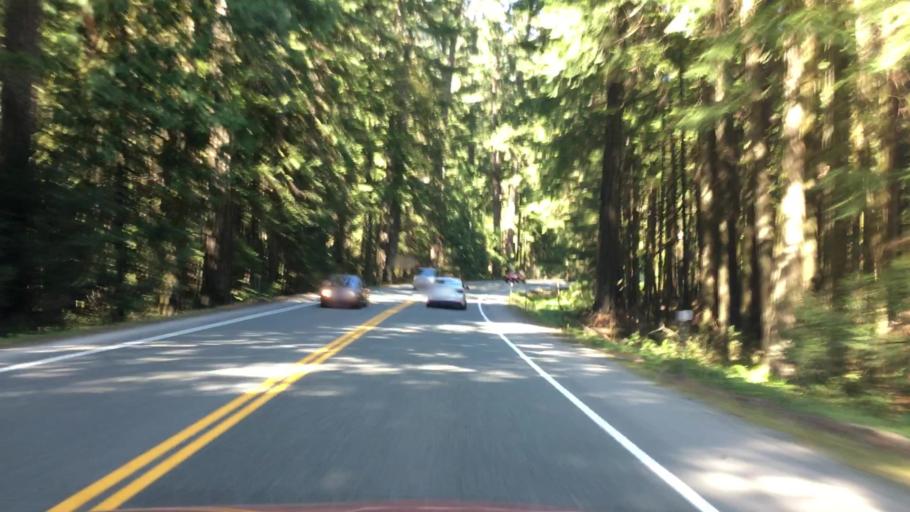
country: CA
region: British Columbia
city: Port Alberni
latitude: 49.2819
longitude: -124.6754
